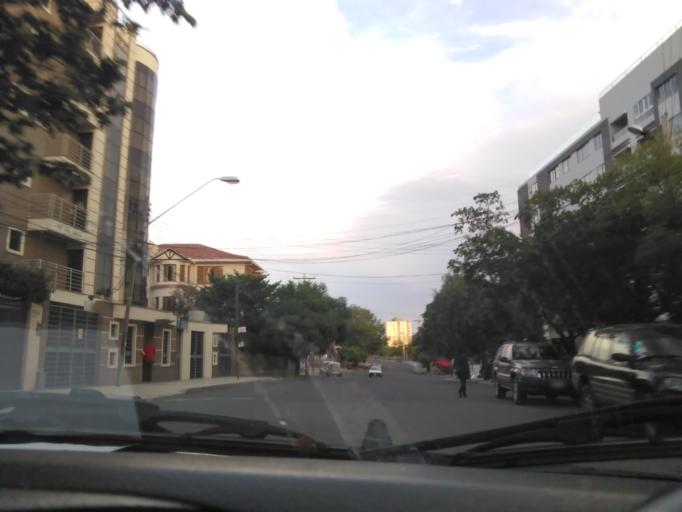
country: BO
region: Cochabamba
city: Cochabamba
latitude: -17.3716
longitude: -66.1433
